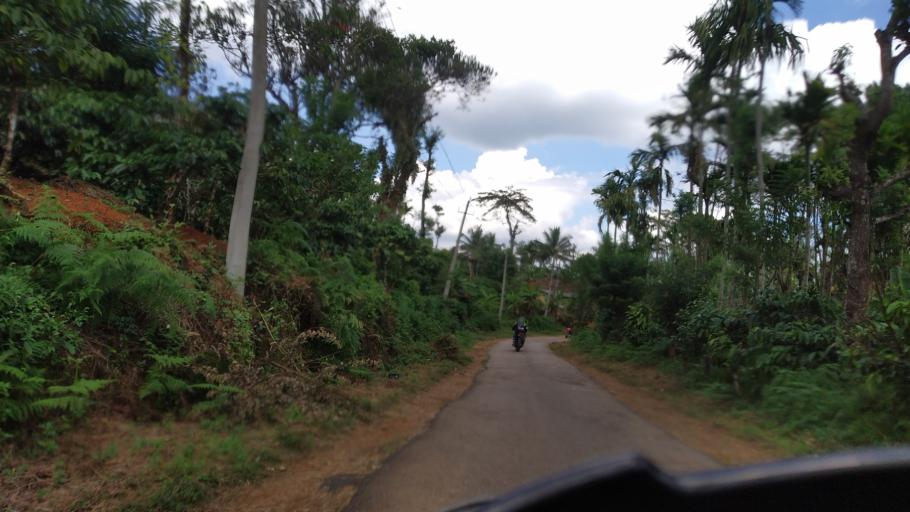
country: IN
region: Karnataka
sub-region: Kodagu
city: Ponnampet
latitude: 12.0354
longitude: 75.9142
